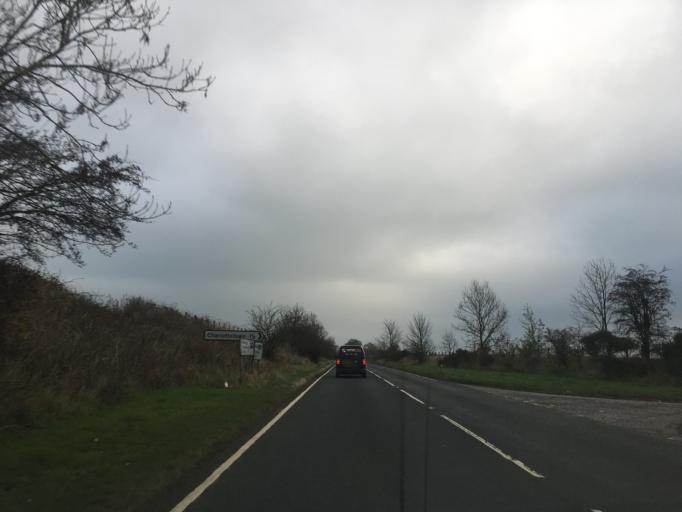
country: GB
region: Scotland
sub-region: Fife
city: Auchtermuchty
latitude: 56.2996
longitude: -3.1874
